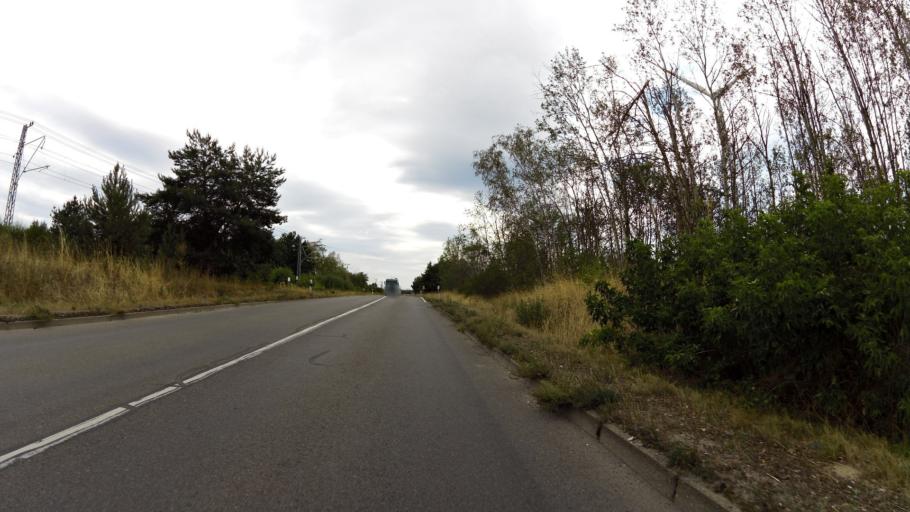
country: DE
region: Brandenburg
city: Heinersbruck
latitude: 51.7969
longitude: 14.4836
